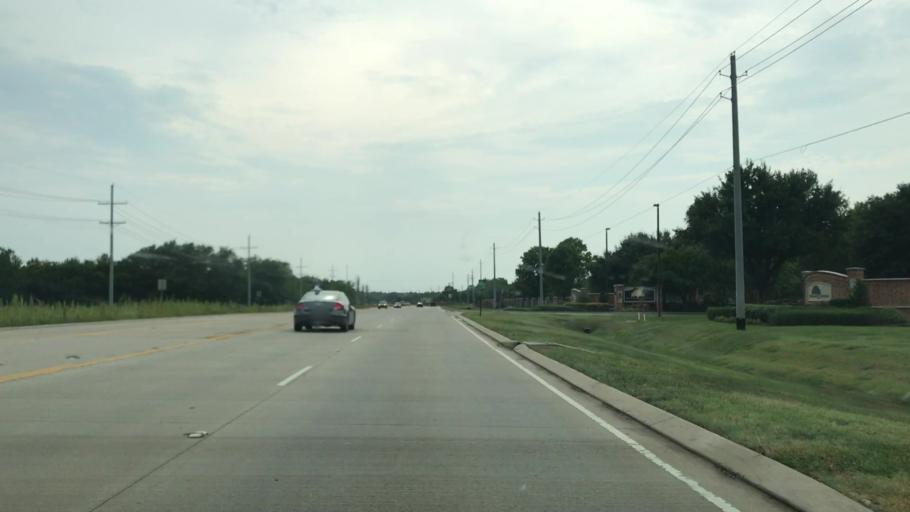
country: US
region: Louisiana
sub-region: Bossier Parish
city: Bossier City
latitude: 32.4009
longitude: -93.7026
